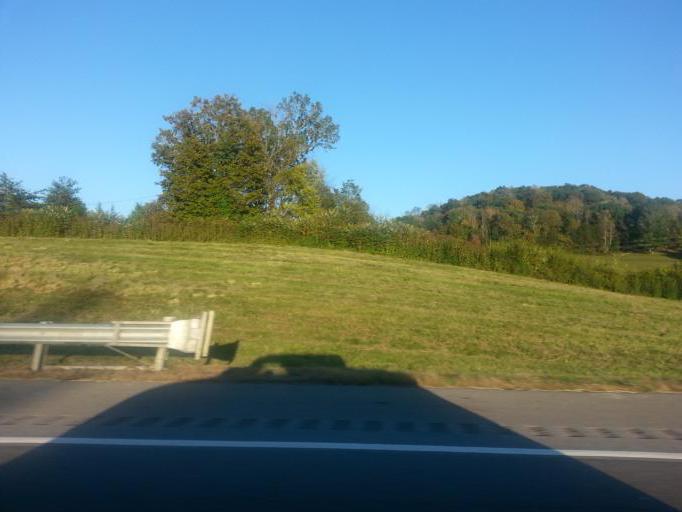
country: US
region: Tennessee
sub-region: Anderson County
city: Norris
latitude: 36.1275
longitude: -84.0356
